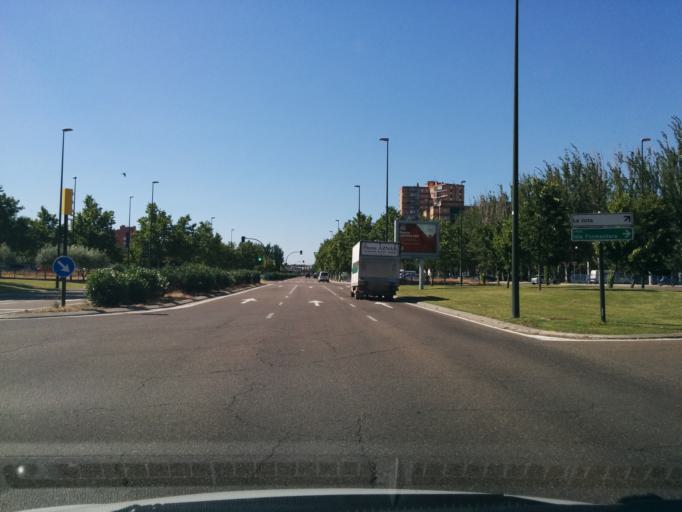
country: ES
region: Aragon
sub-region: Provincia de Zaragoza
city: Zaragoza
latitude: 41.6619
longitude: -0.8556
